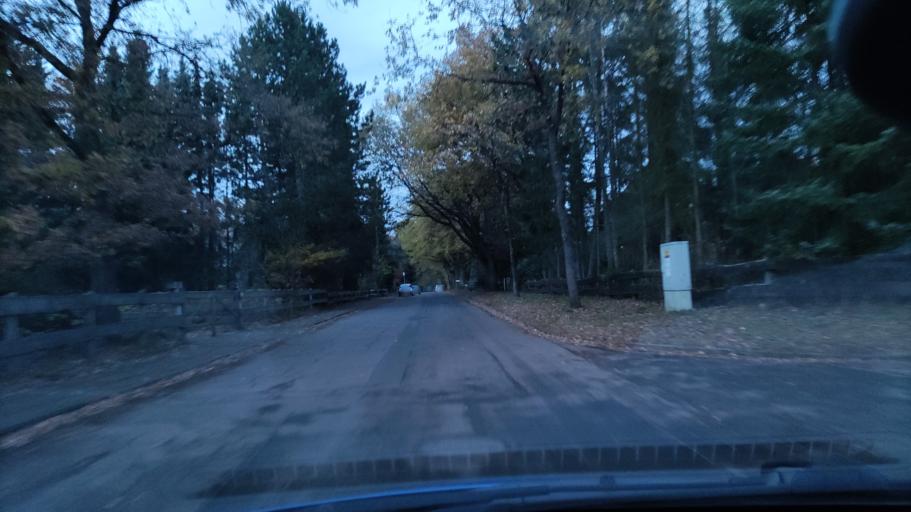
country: DE
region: Lower Saxony
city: Egestorf
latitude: 53.1610
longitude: 10.0349
